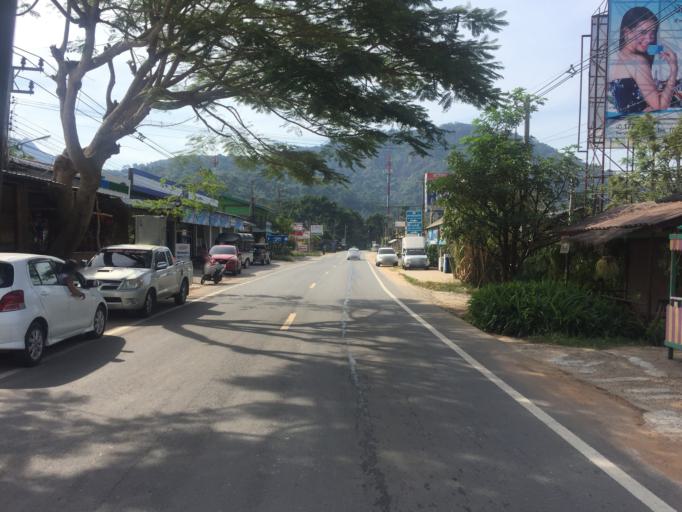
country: TH
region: Trat
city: Laem Ngop
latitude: 12.1347
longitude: 102.2760
